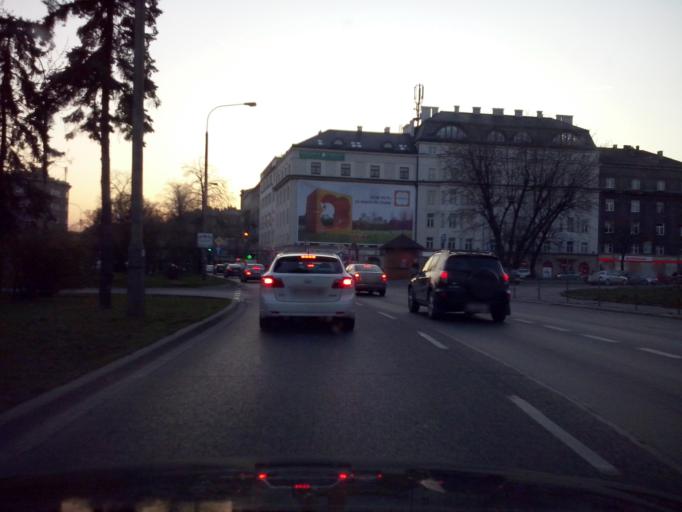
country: PL
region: Lesser Poland Voivodeship
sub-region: Krakow
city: Krakow
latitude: 50.0739
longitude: 19.9370
